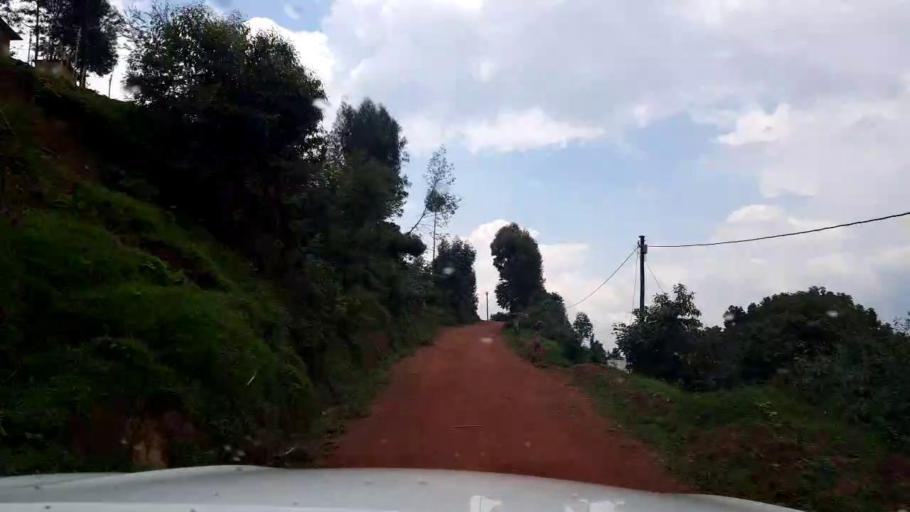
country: RW
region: Northern Province
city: Byumba
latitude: -1.5270
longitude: 29.9580
